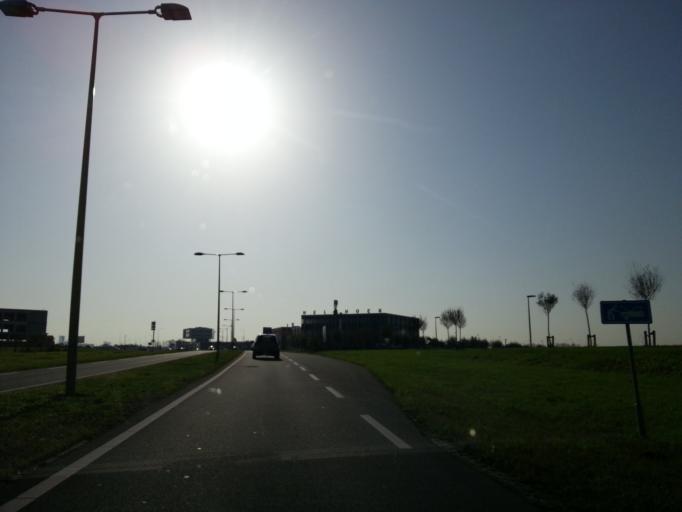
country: NL
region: South Holland
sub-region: Gemeente Lansingerland
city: Berkel en Rodenrijs
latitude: 51.9845
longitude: 4.4480
